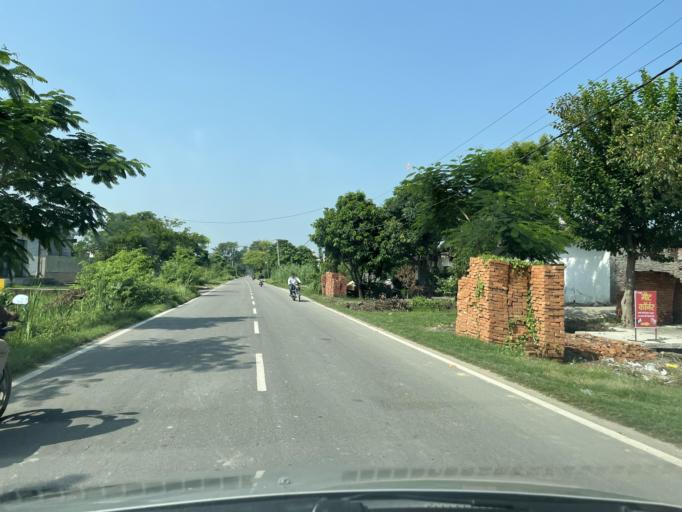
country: IN
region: Uttarakhand
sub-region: Udham Singh Nagar
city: Bazpur
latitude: 29.2020
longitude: 79.2053
